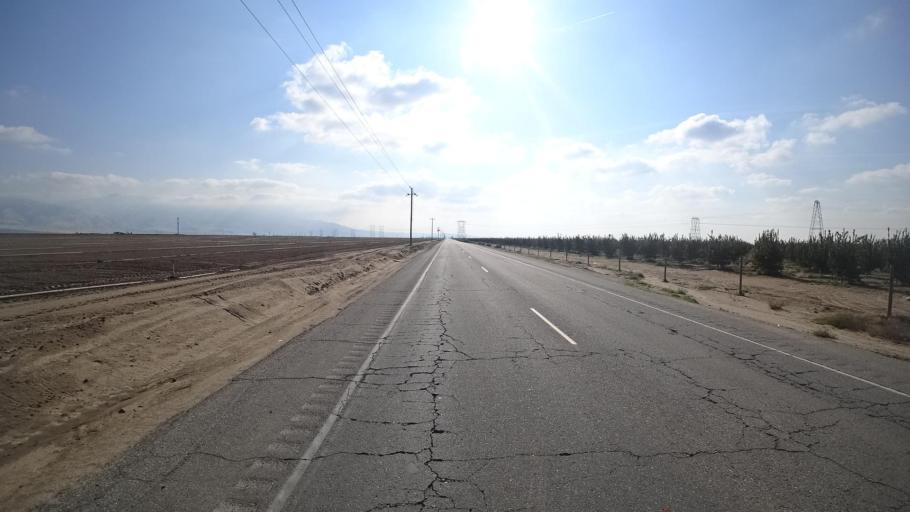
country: US
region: California
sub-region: Kern County
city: Arvin
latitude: 35.2598
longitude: -118.8248
